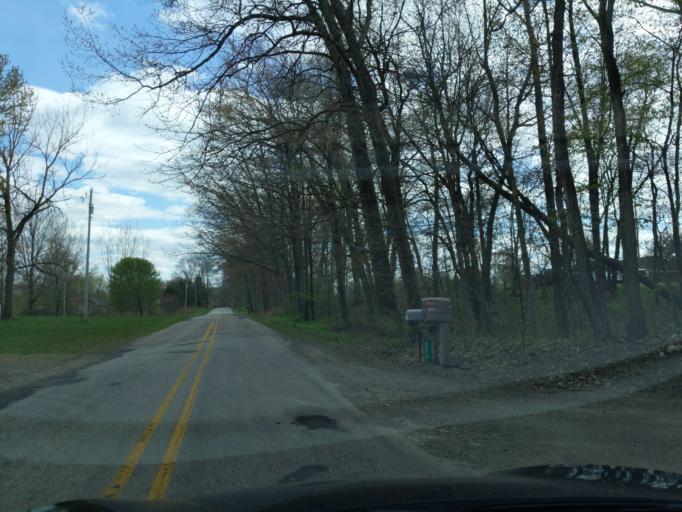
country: US
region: Michigan
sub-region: Ingham County
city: Leslie
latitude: 42.4577
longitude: -84.5460
